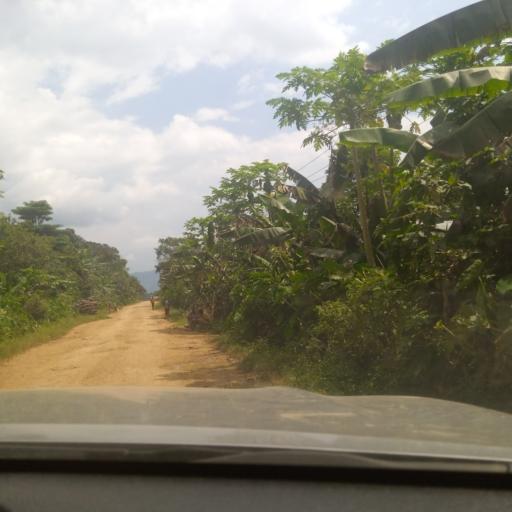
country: ET
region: Southern Nations, Nationalities, and People's Region
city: Tippi
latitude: 7.1349
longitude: 35.4243
